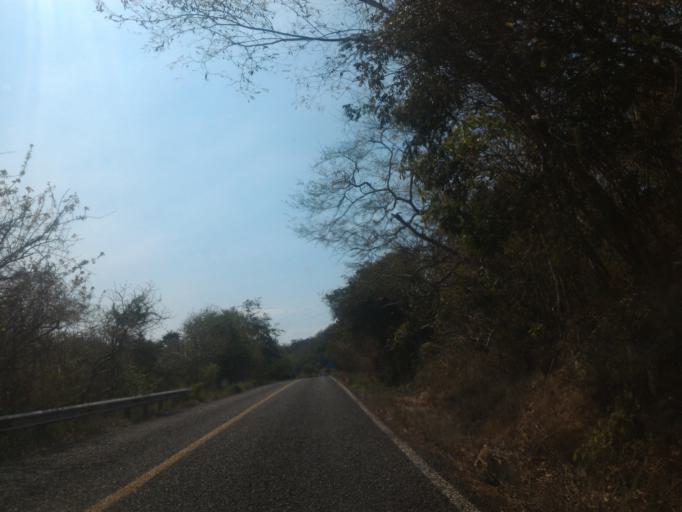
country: MX
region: Michoacan
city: Coahuayana Viejo
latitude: 18.3713
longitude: -103.5090
